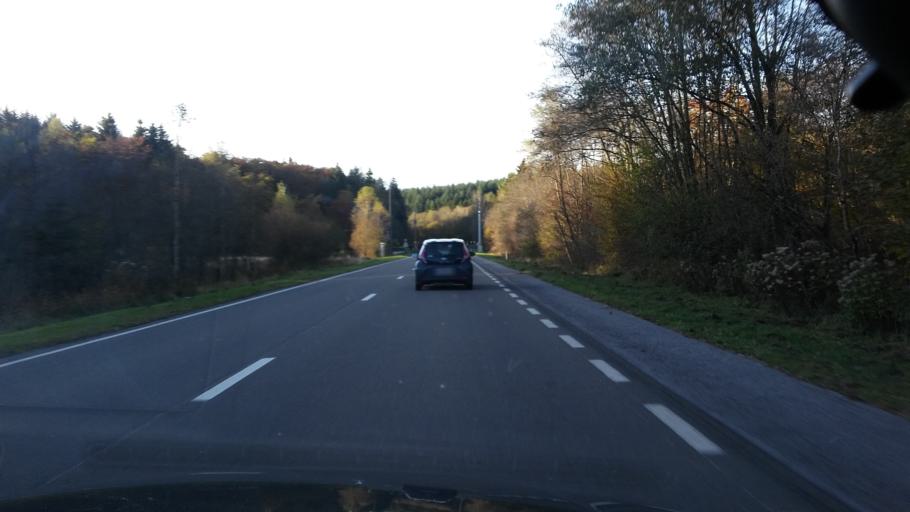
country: BE
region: Wallonia
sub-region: Province du Luxembourg
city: Bouillon
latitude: 49.7606
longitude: 5.1366
